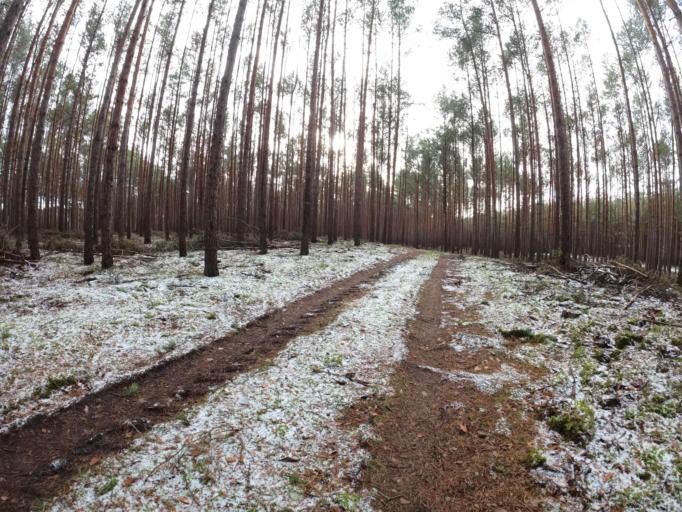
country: PL
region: Lubusz
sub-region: Powiat slubicki
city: Cybinka
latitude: 52.2549
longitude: 14.7985
